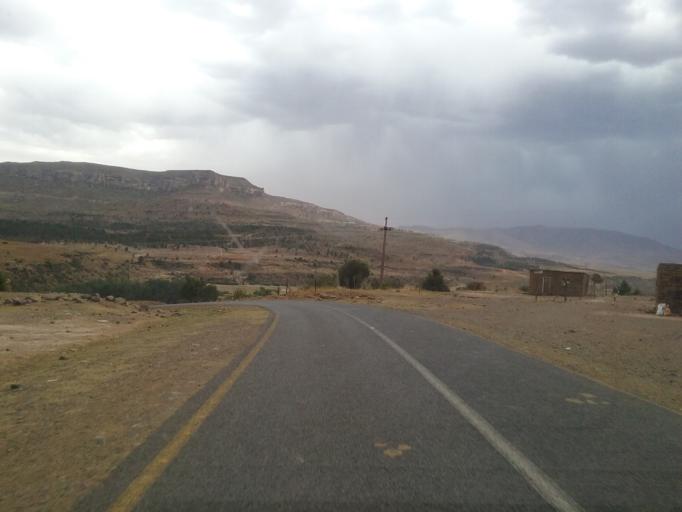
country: LS
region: Quthing
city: Quthing
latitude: -30.2850
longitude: 27.8084
